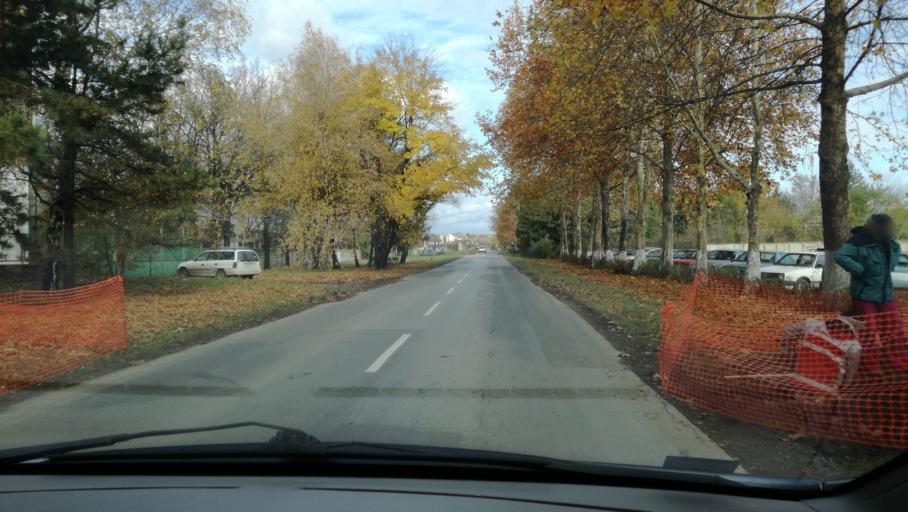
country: RS
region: Autonomna Pokrajina Vojvodina
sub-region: Severnobanatski Okrug
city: Kikinda
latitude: 45.8107
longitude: 20.4475
